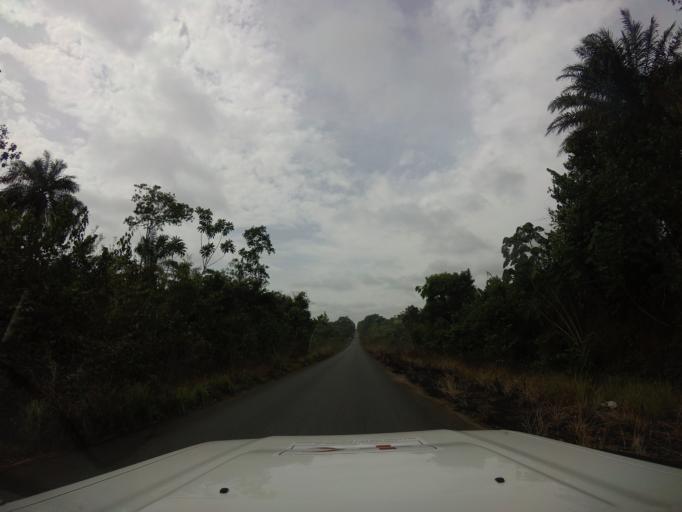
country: LR
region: Bomi
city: Tubmanburg
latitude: 6.7292
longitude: -10.8630
